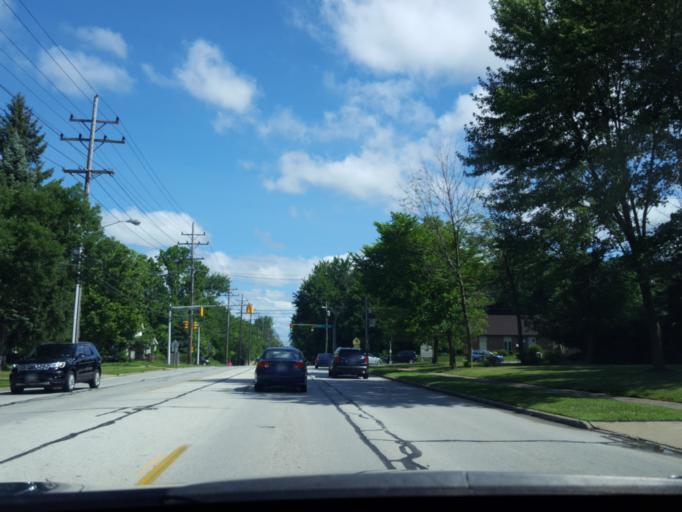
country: US
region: Ohio
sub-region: Cuyahoga County
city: Lyndhurst
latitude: 41.5301
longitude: -81.4972
